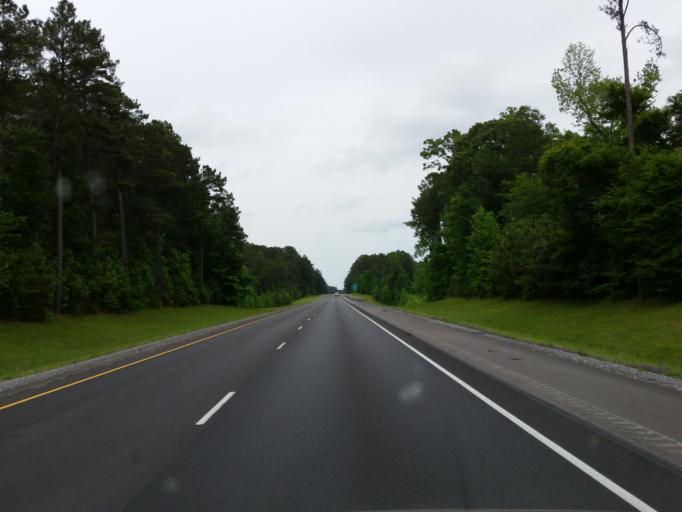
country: US
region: Mississippi
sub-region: Jones County
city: Sharon
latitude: 31.9476
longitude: -88.9831
